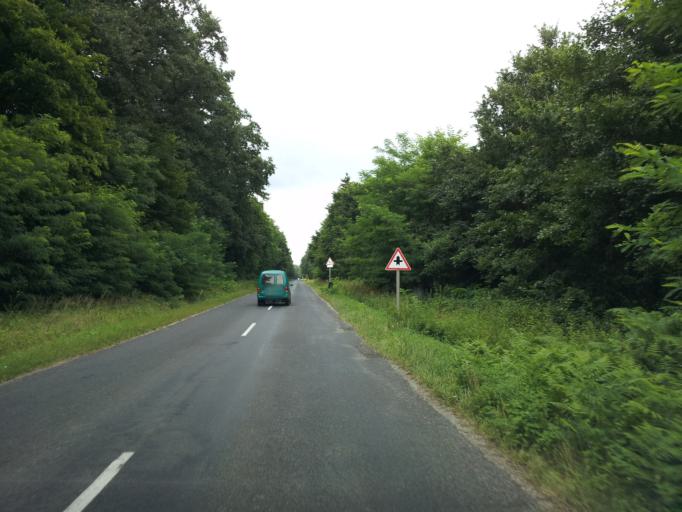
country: HU
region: Zala
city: Turje
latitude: 47.0606
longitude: 17.0177
